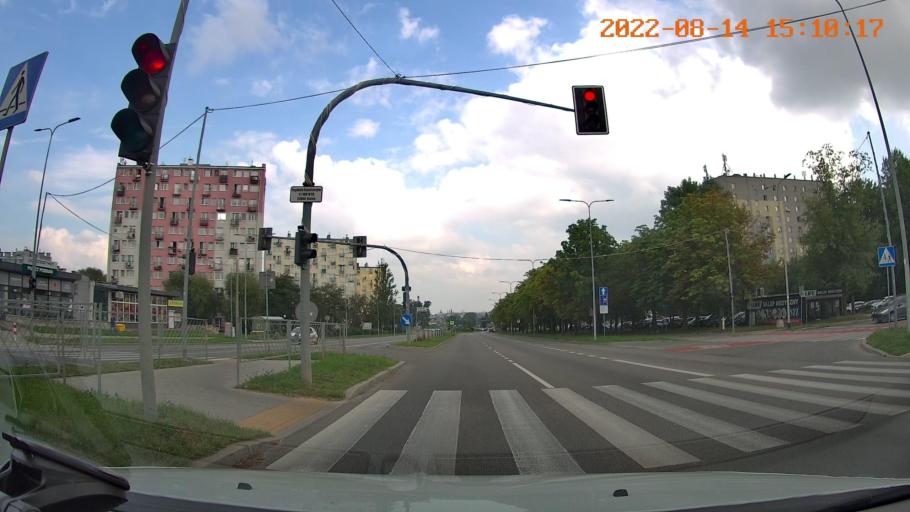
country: PL
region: Swietokrzyskie
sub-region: Powiat kielecki
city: Kielce
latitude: 50.8748
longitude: 20.6024
